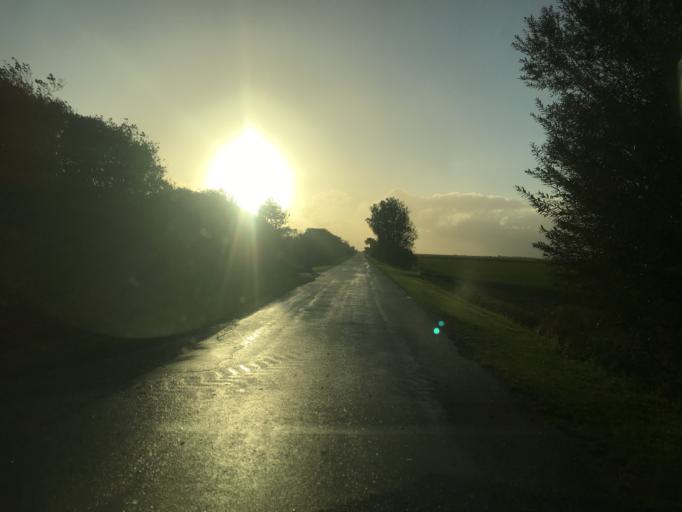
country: DE
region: Schleswig-Holstein
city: Aventoft
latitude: 54.9470
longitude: 8.7557
